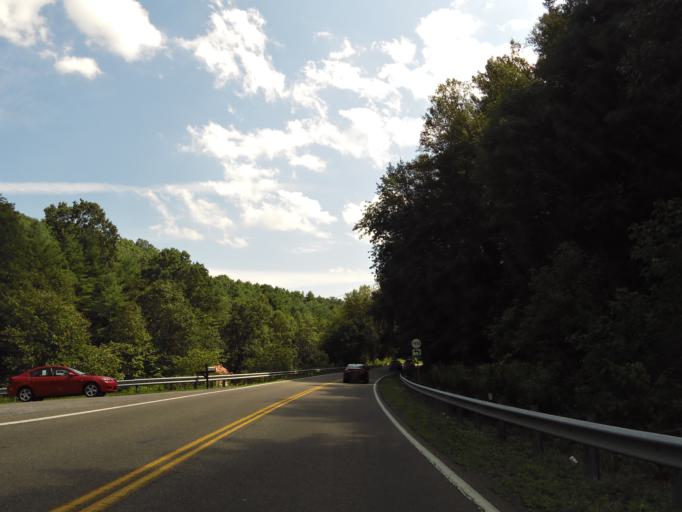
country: US
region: Virginia
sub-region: Washington County
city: Abingdon
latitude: 36.6850
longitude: -81.9722
